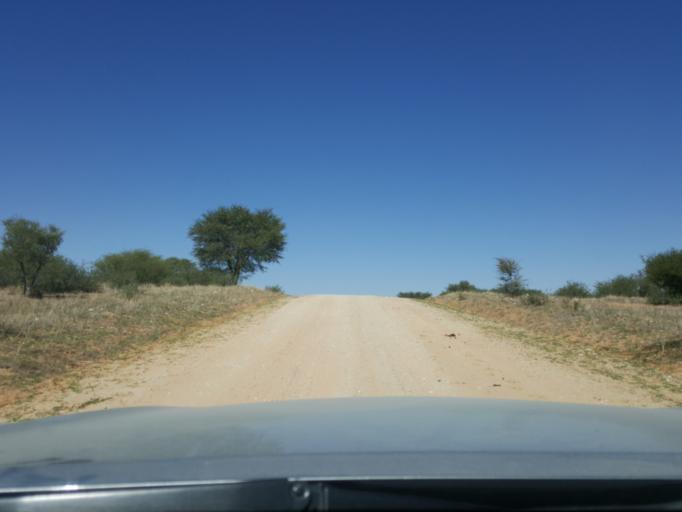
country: BW
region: Kgalagadi
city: Hukuntsi
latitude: -24.1060
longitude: 21.2322
